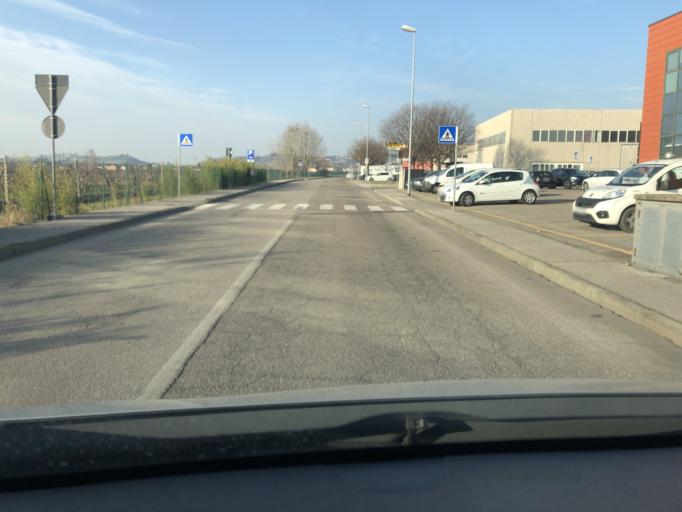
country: IT
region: Veneto
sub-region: Provincia di Verona
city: Lugagnano
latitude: 45.4366
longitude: 10.8673
